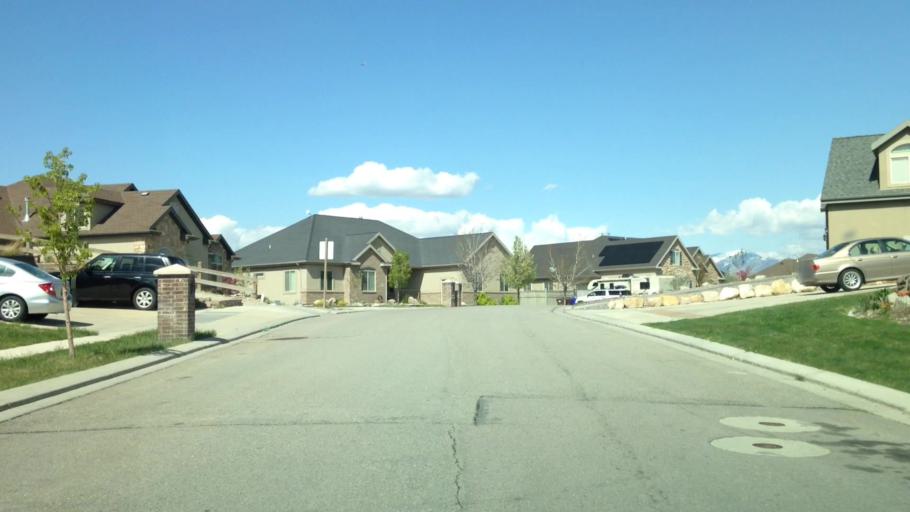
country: US
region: Utah
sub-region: Utah County
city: Saratoga Springs
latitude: 40.3783
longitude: -111.9669
